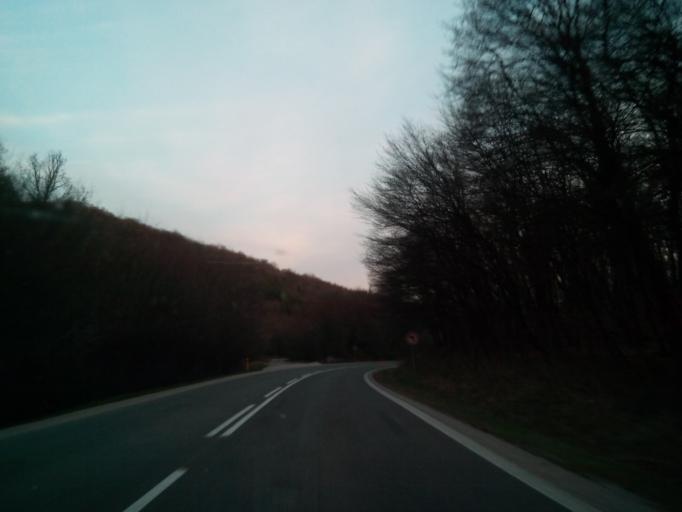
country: SK
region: Kosicky
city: Roznava
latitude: 48.6087
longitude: 20.6373
